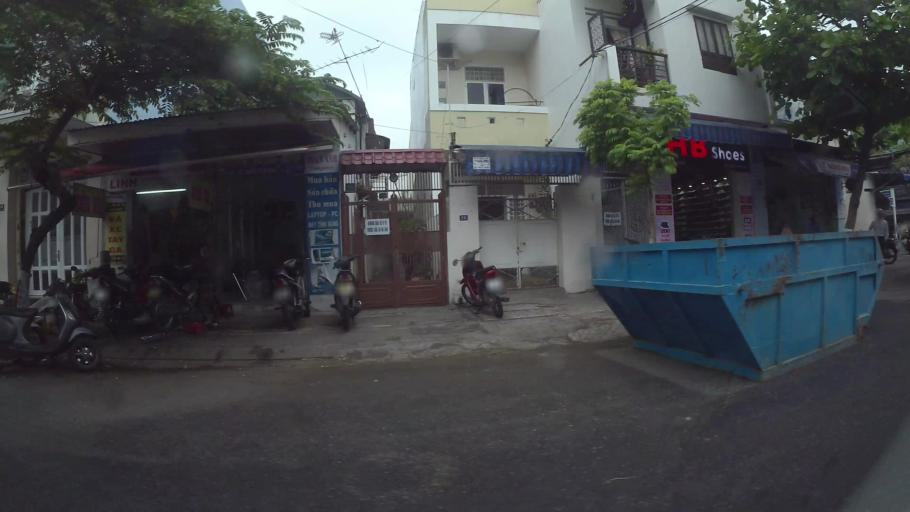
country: VN
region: Da Nang
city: Da Nang
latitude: 16.0758
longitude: 108.2149
